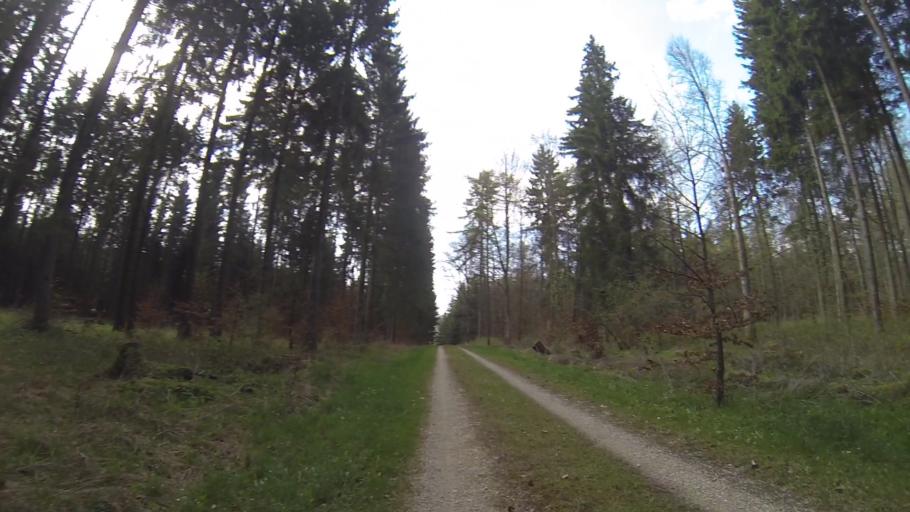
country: DE
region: Baden-Wuerttemberg
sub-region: Regierungsbezirk Stuttgart
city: Nattheim
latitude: 48.6762
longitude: 10.2131
